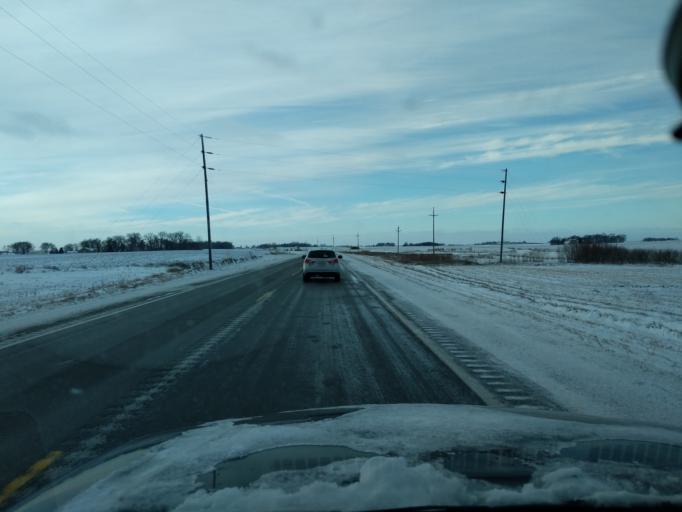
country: US
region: Minnesota
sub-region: Renville County
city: Hector
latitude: 44.7366
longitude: -94.6339
